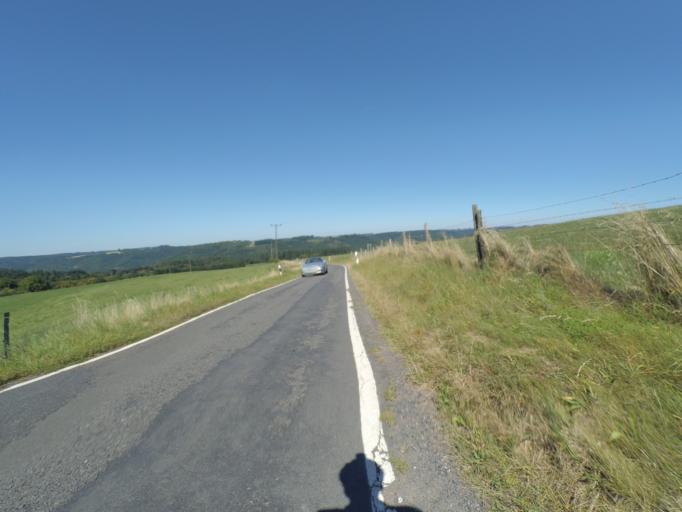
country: DE
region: Rheinland-Pfalz
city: Bad Bertrich
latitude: 50.0603
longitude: 7.0284
